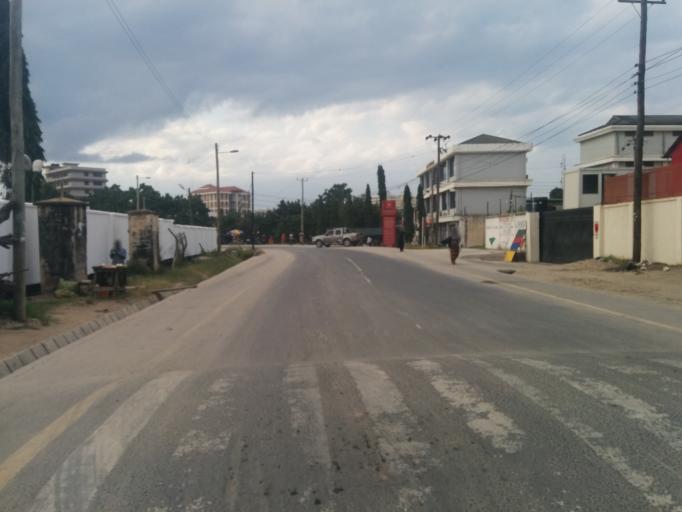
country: TZ
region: Dar es Salaam
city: Dar es Salaam
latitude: -6.8314
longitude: 39.2756
